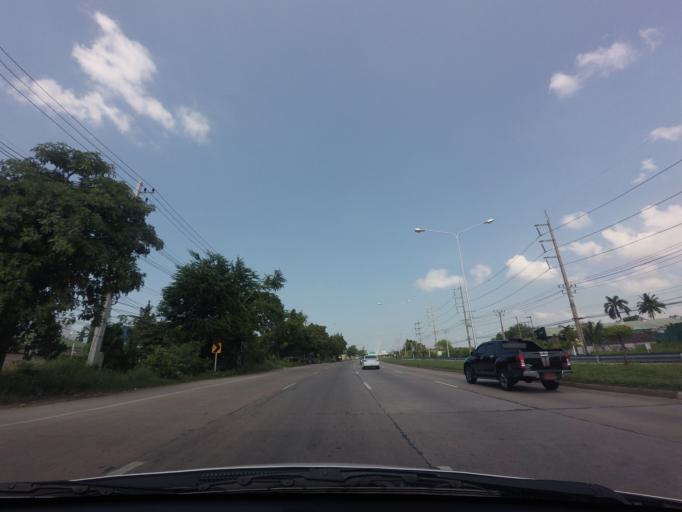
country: TH
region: Nakhon Pathom
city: Sam Phran
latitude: 13.7588
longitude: 100.1878
